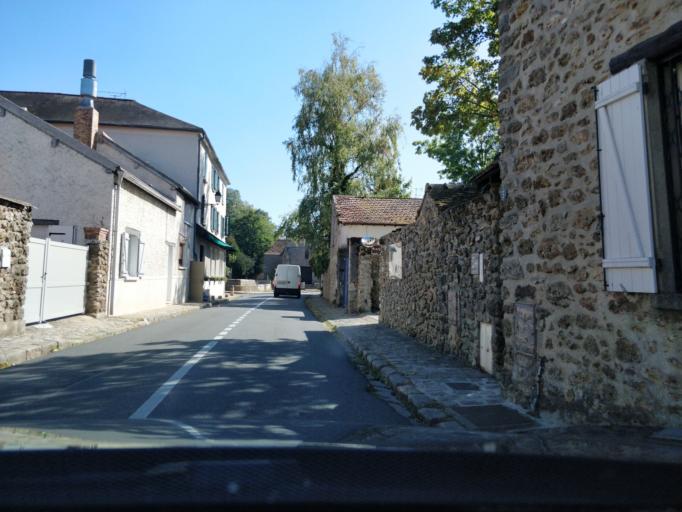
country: FR
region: Ile-de-France
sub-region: Departement de l'Essonne
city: Fontenay-les-Briis
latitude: 48.6482
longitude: 2.1526
